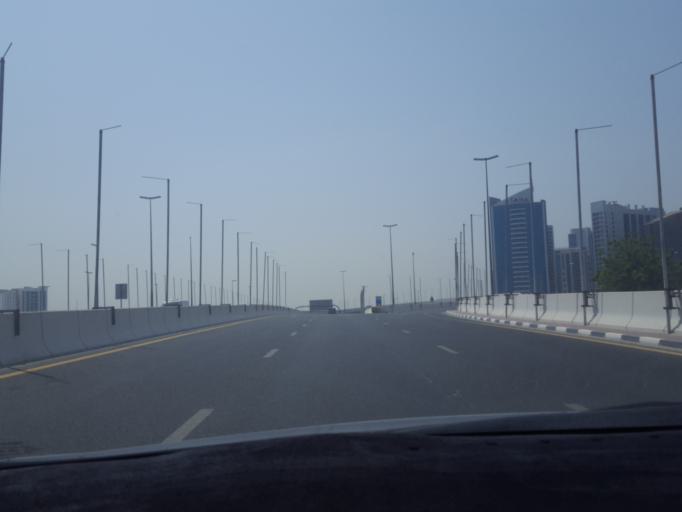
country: AE
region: Dubai
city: Dubai
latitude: 25.1064
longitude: 55.1756
